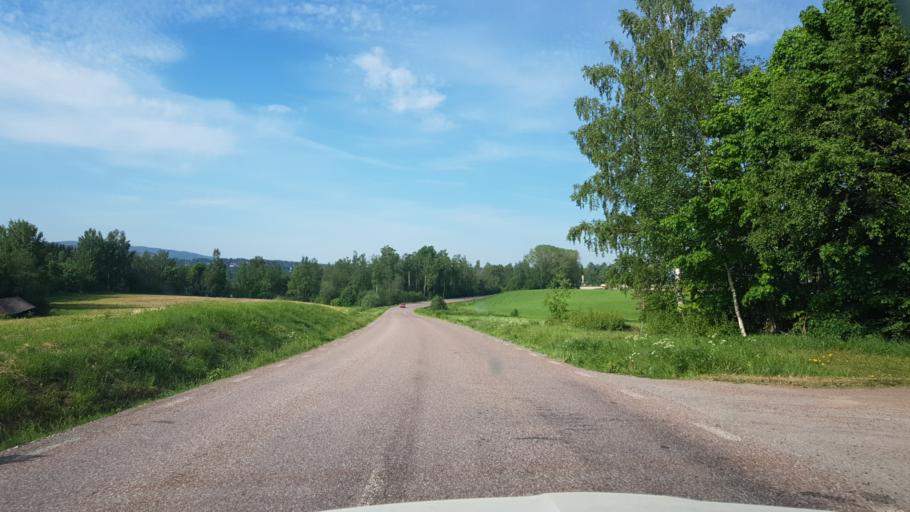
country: SE
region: Dalarna
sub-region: Borlange Kommun
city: Ornas
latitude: 60.4257
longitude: 15.6336
